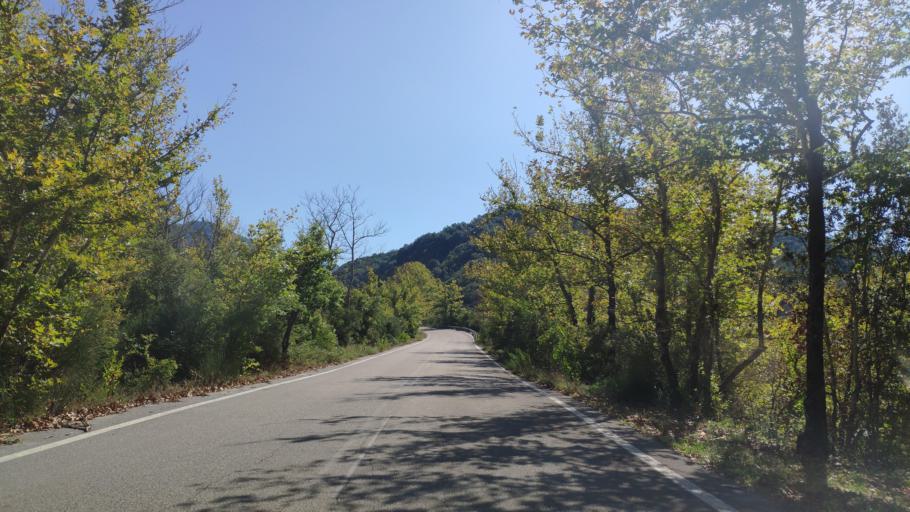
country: GR
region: West Greece
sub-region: Nomos Aitolias kai Akarnanias
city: Sardinia
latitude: 38.9237
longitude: 21.3751
